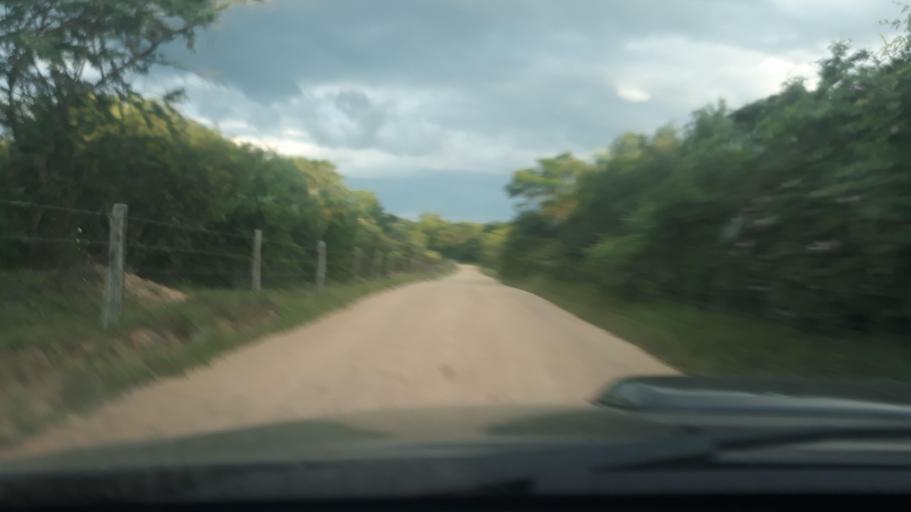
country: BR
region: Bahia
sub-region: Riacho De Santana
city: Riacho de Santana
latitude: -13.9094
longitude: -42.9428
